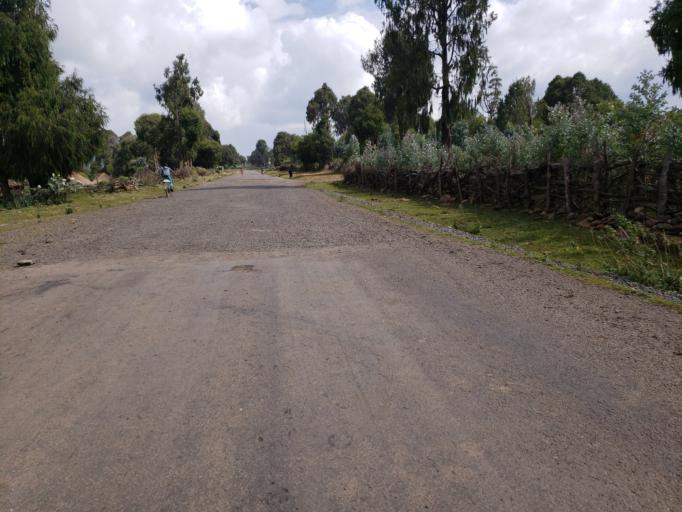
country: ET
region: Oromiya
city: Dodola
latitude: 6.8670
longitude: 39.3898
